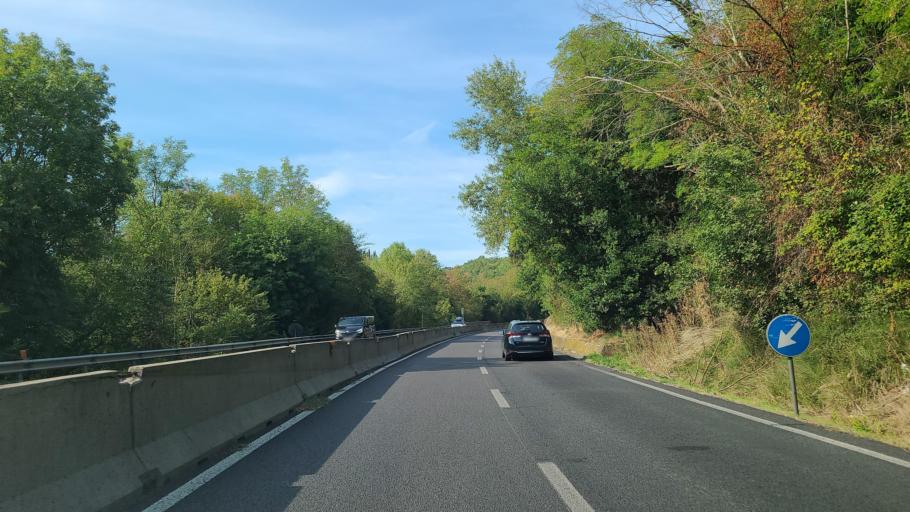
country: IT
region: Tuscany
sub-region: Province of Florence
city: San Casciano in Val di Pesa
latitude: 43.6596
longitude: 11.2038
